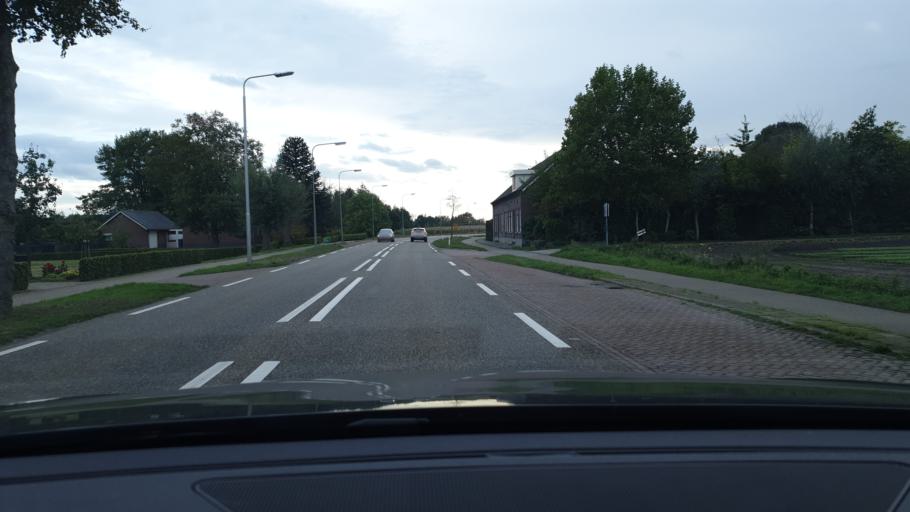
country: NL
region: Limburg
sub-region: Gemeente Peel en Maas
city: Maasbree
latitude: 51.4329
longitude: 6.0462
